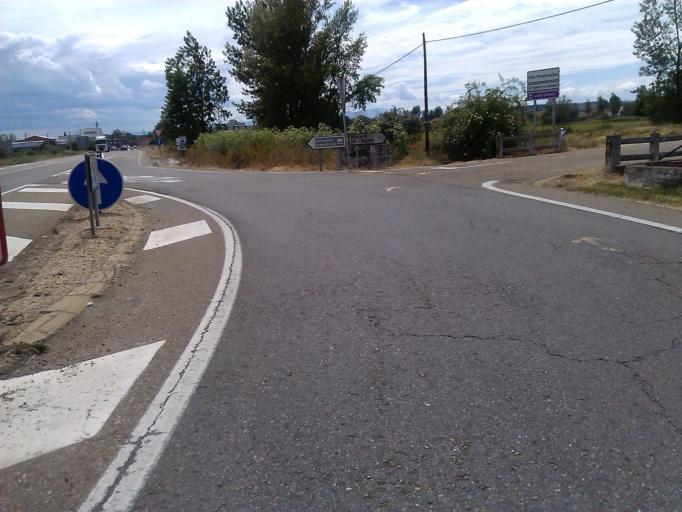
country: ES
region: Castille and Leon
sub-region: Provincia de Leon
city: Hospital de Orbigo
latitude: 42.4626
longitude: -5.8699
